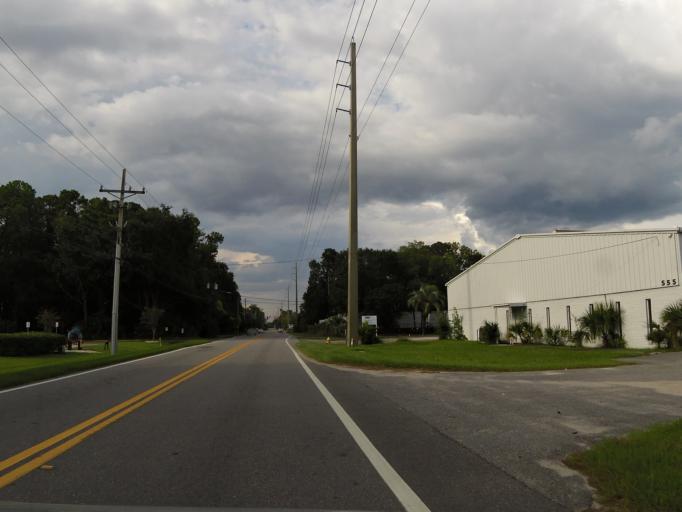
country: US
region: Florida
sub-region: Duval County
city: Jacksonville
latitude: 30.3337
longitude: -81.7435
